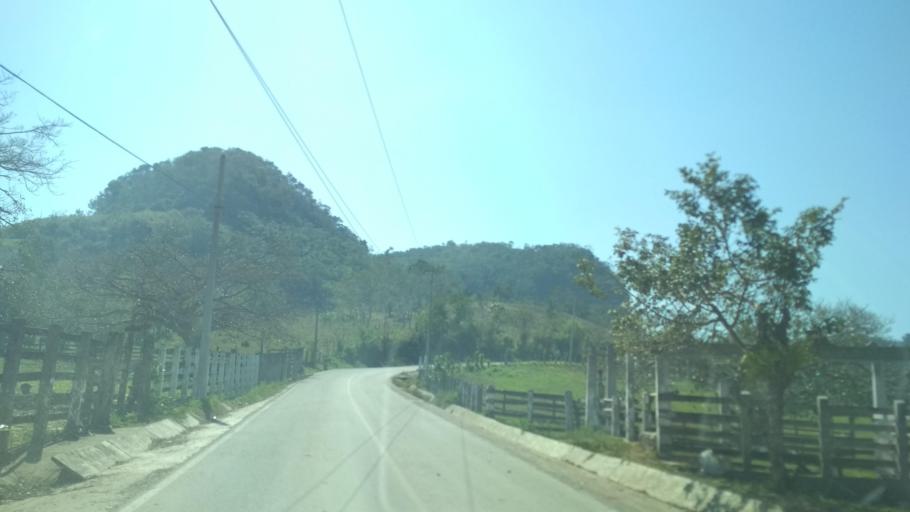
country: MX
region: Veracruz
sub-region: Papantla
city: Polutla
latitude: 20.4757
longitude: -97.2101
